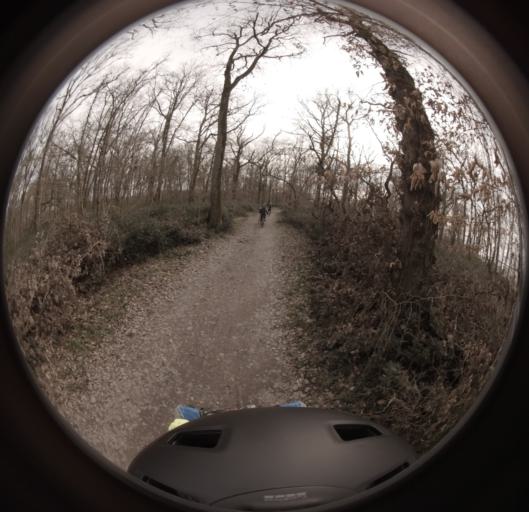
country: FR
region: Midi-Pyrenees
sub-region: Departement du Tarn-et-Garonne
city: Montech
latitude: 43.9597
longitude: 1.2592
